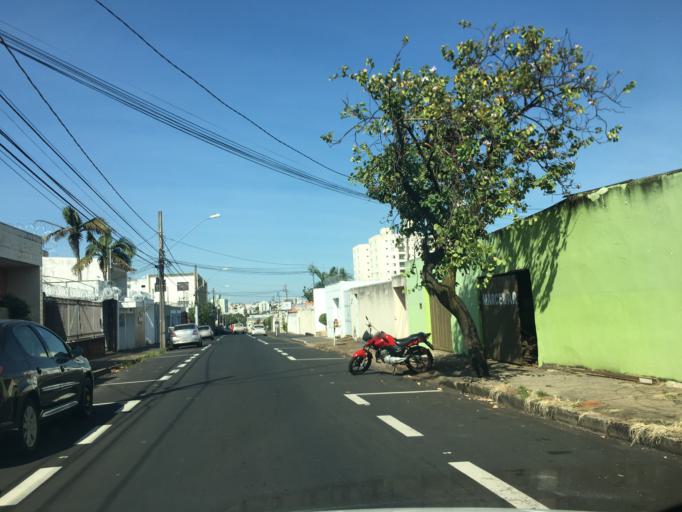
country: BR
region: Minas Gerais
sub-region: Uberlandia
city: Uberlandia
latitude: -18.8980
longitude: -48.2644
